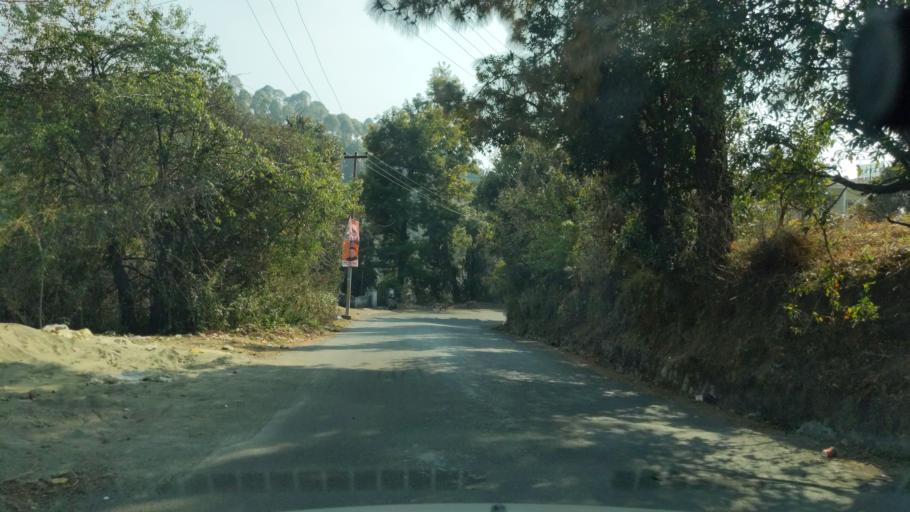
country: IN
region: Uttarakhand
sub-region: Naini Tal
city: Bhowali
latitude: 29.3900
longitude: 79.5315
